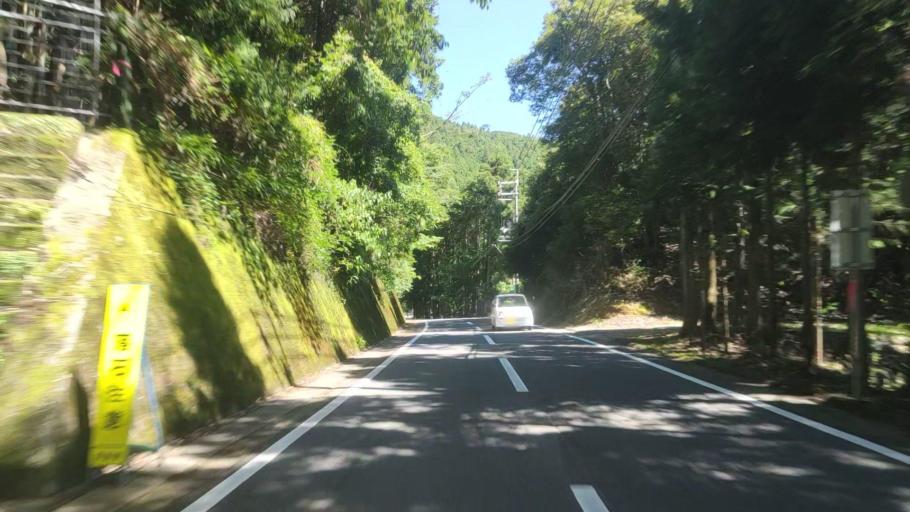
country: JP
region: Nara
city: Yoshino-cho
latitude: 34.3838
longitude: 135.9101
